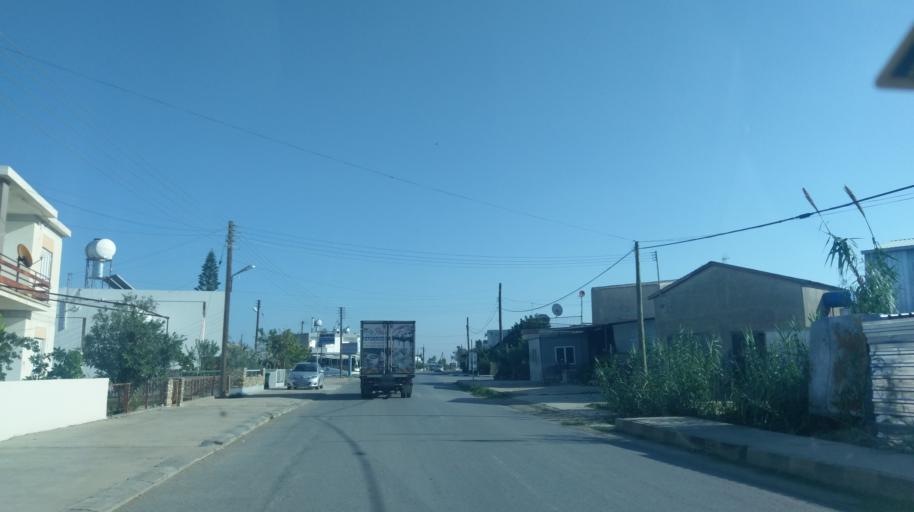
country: CY
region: Larnaka
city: Pergamos
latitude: 35.1085
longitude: 33.6886
